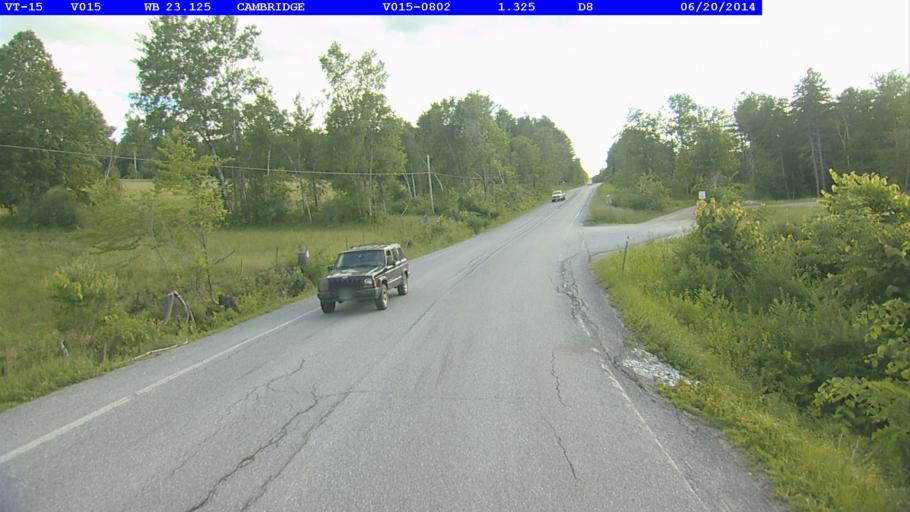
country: US
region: Vermont
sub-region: Chittenden County
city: Jericho
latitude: 44.6407
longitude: -72.8938
